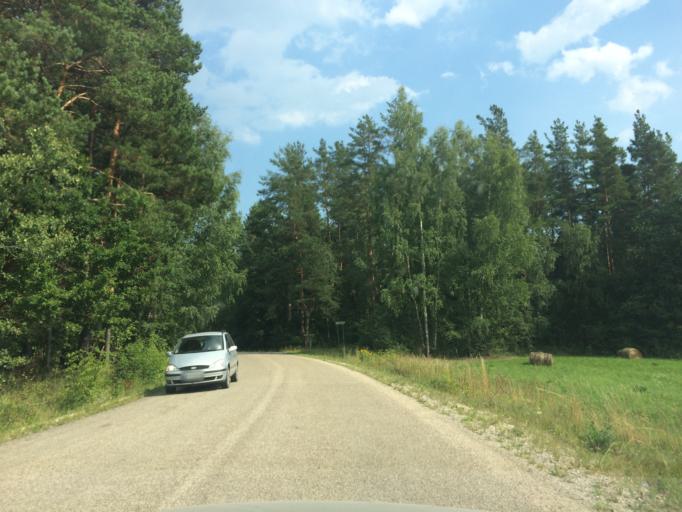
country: LV
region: Rezekne
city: Rezekne
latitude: 56.5492
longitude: 27.3624
